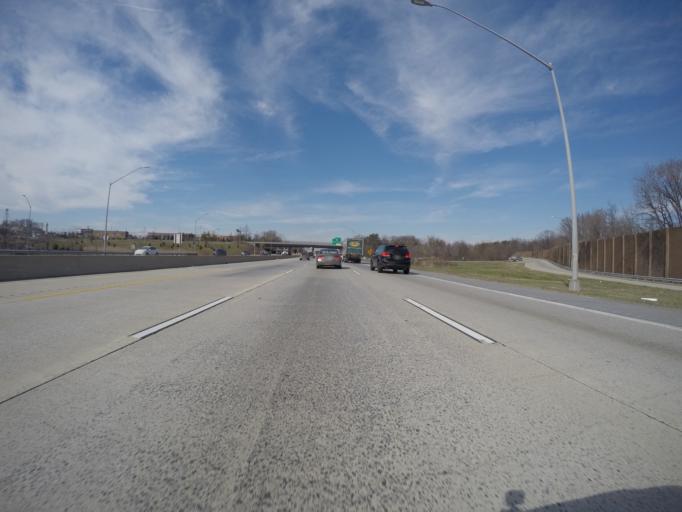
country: US
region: Maryland
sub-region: Anne Arundel County
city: South Gate
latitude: 39.1410
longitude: -76.6441
